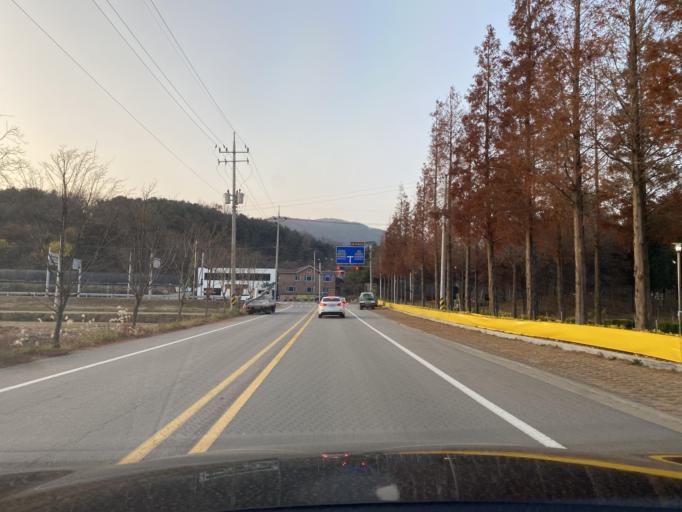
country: KR
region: Chungcheongnam-do
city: Hongsung
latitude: 36.6889
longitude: 126.6571
